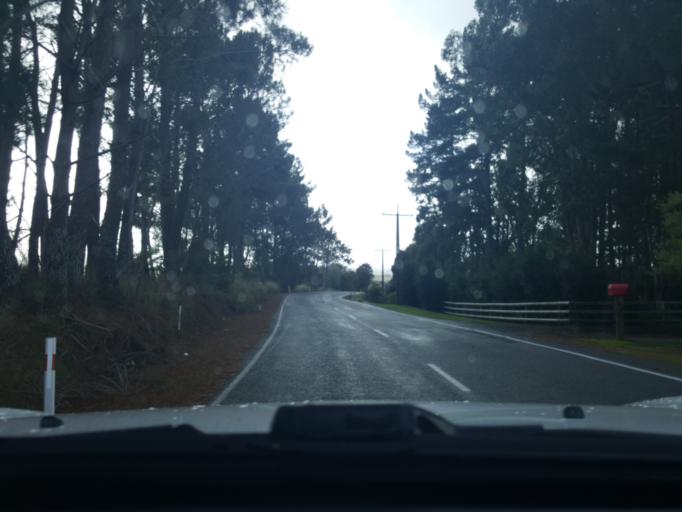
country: NZ
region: Waikato
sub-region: Waikato District
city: Te Kauwhata
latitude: -37.4453
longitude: 175.0831
